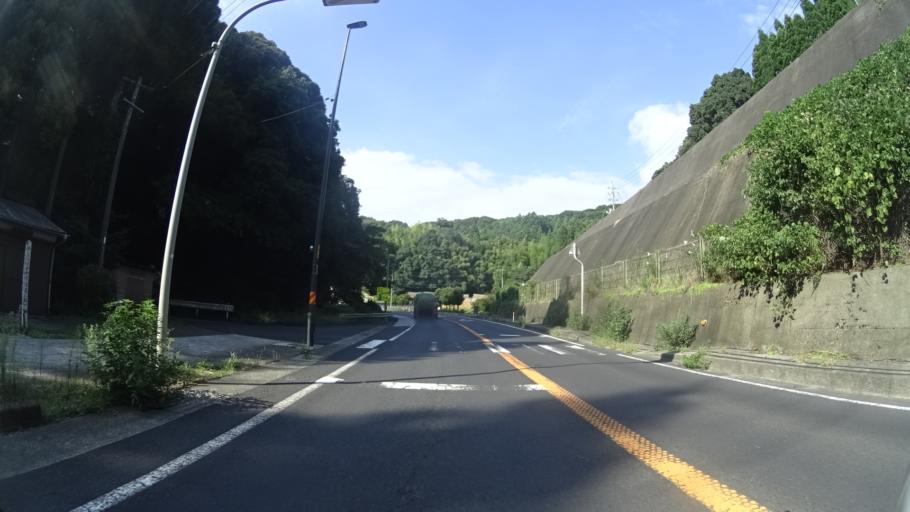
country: JP
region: Shimane
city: Odacho-oda
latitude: 35.2532
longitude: 132.5711
